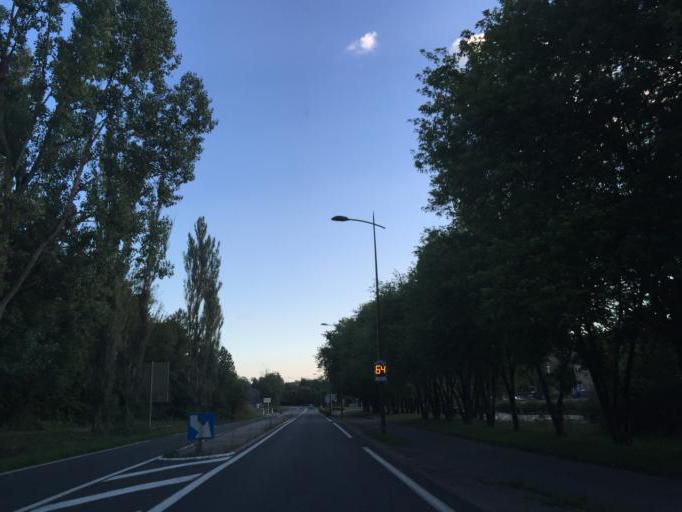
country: FR
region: Midi-Pyrenees
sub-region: Departement de l'Aveyron
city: Rodez
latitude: 44.3791
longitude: 2.5659
